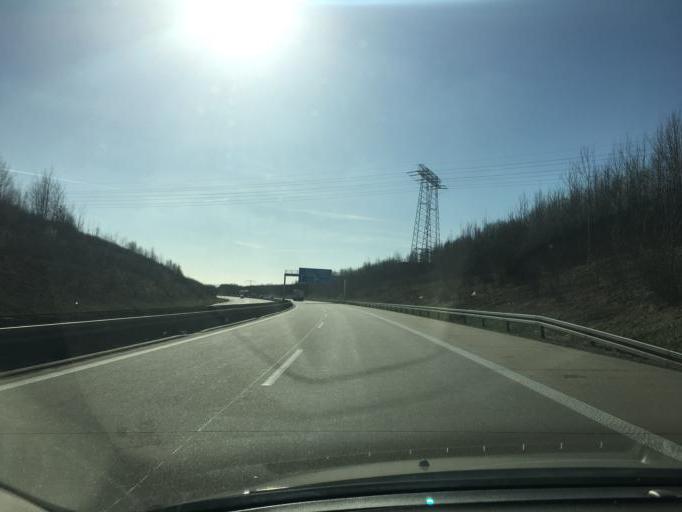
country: DE
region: Saxony
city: Hartmannsdorf
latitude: 50.8573
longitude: 12.8223
